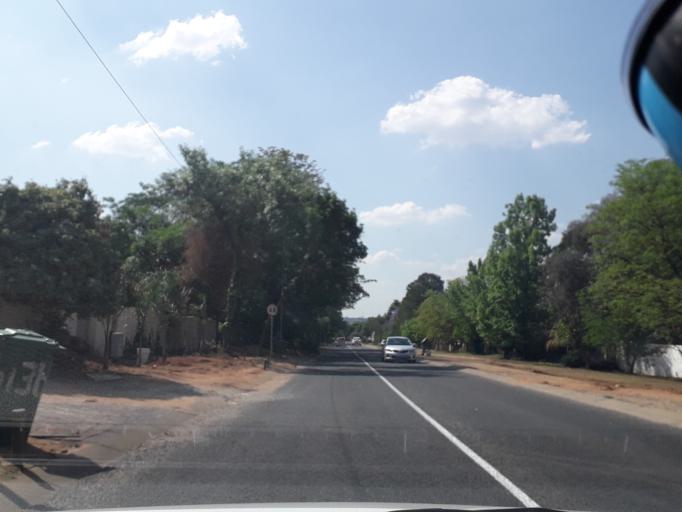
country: ZA
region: Gauteng
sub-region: City of Johannesburg Metropolitan Municipality
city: Modderfontein
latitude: -26.0809
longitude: 28.0499
